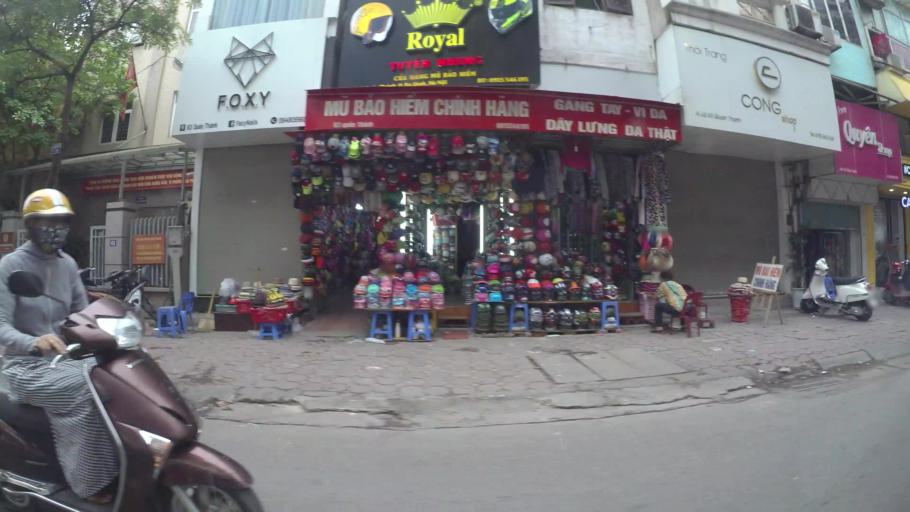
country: VN
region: Ha Noi
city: Hoan Kiem
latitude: 21.0424
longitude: 105.8422
